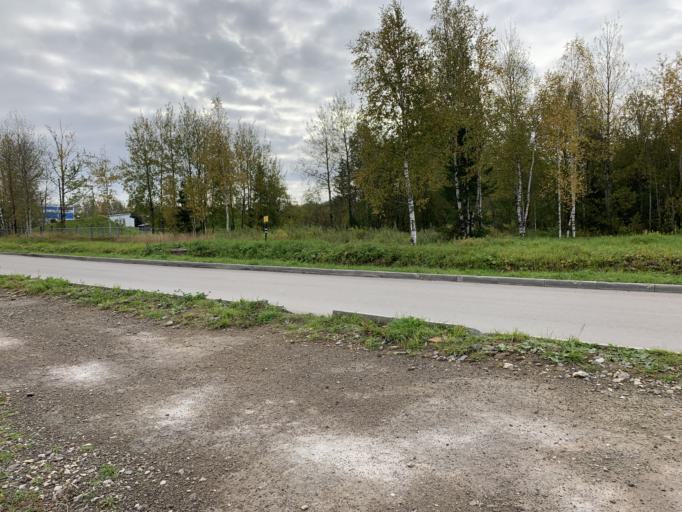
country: RU
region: Perm
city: Gubakha
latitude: 58.8337
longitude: 57.5574
